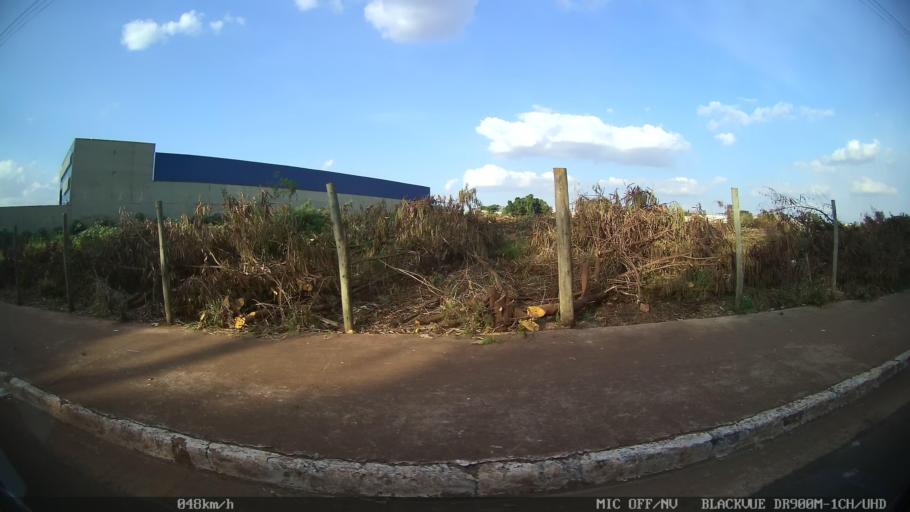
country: BR
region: Sao Paulo
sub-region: Ribeirao Preto
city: Ribeirao Preto
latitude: -21.1393
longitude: -47.8030
